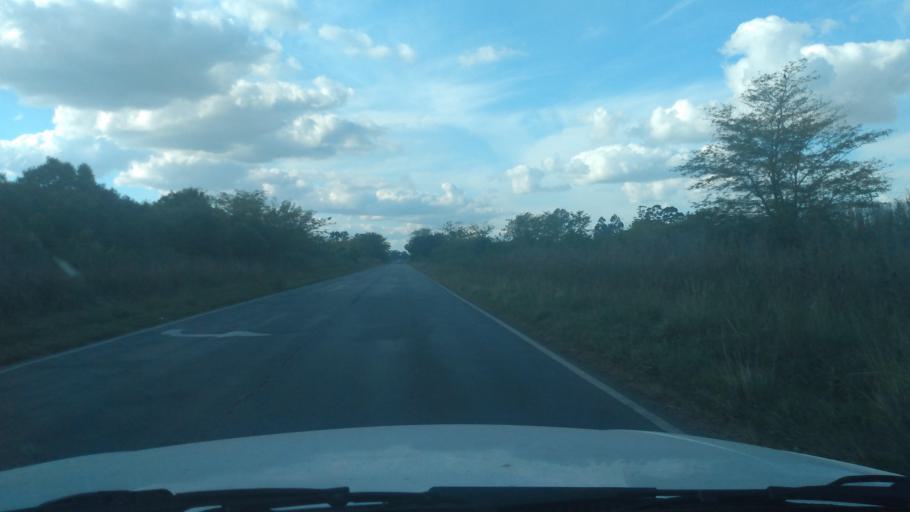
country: AR
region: Buenos Aires
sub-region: Partido de Mercedes
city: Mercedes
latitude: -34.6820
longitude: -59.4044
